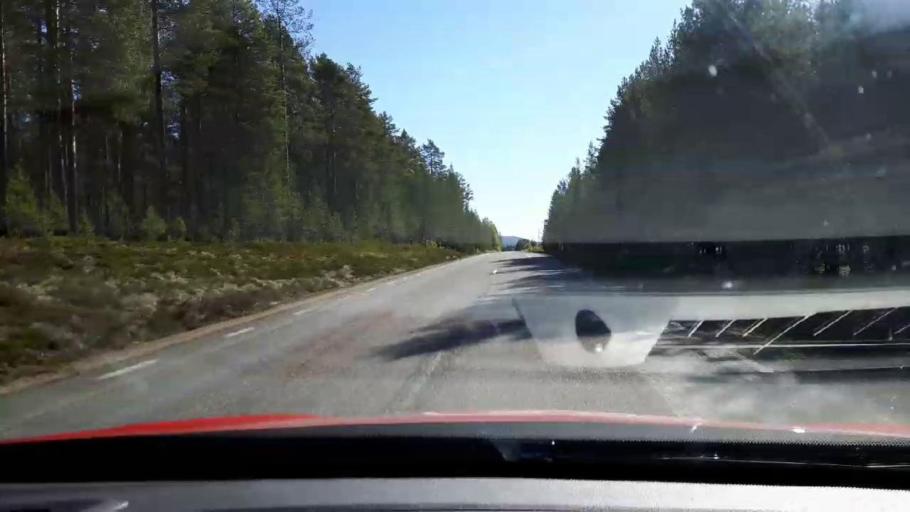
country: SE
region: Jaemtland
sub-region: Harjedalens Kommun
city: Sveg
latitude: 62.3068
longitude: 14.0483
